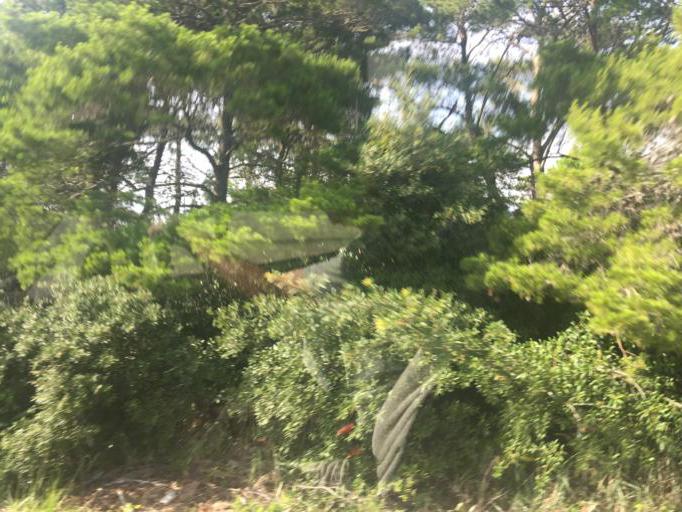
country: US
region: Florida
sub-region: Bay County
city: Laguna Beach
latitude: 30.2568
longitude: -85.9558
